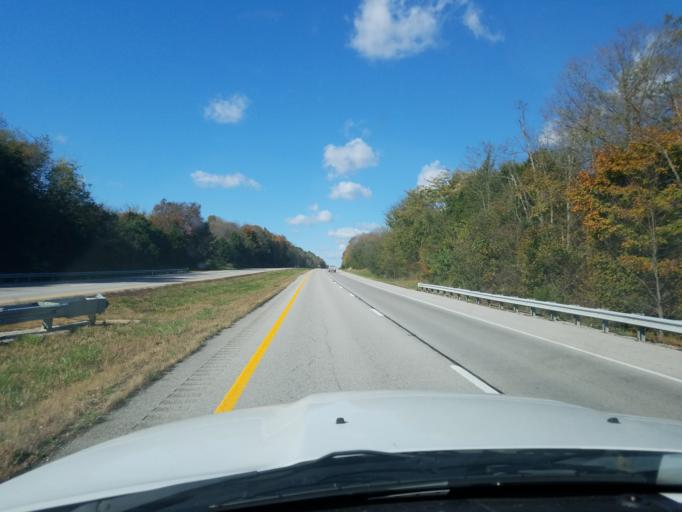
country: US
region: Kentucky
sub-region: Barren County
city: Glasgow
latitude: 36.9964
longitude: -85.8246
